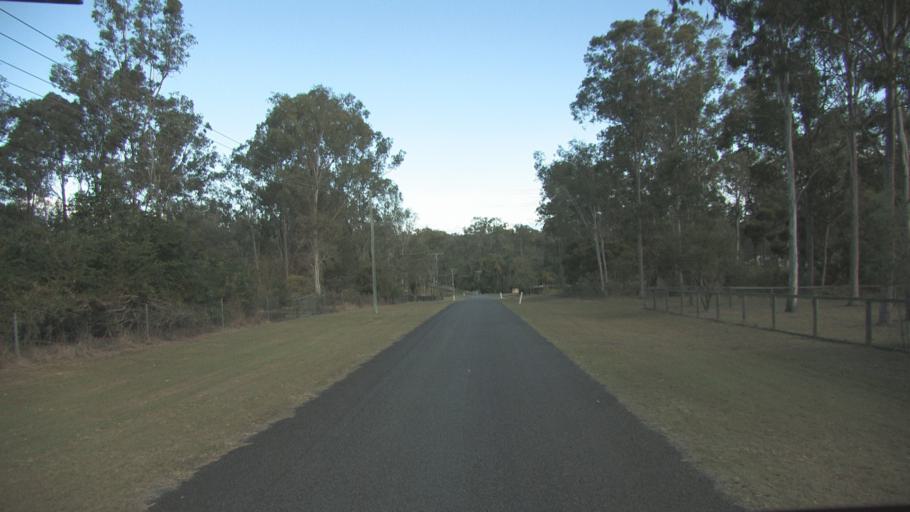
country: AU
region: Queensland
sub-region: Logan
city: North Maclean
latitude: -27.8193
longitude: 153.0528
